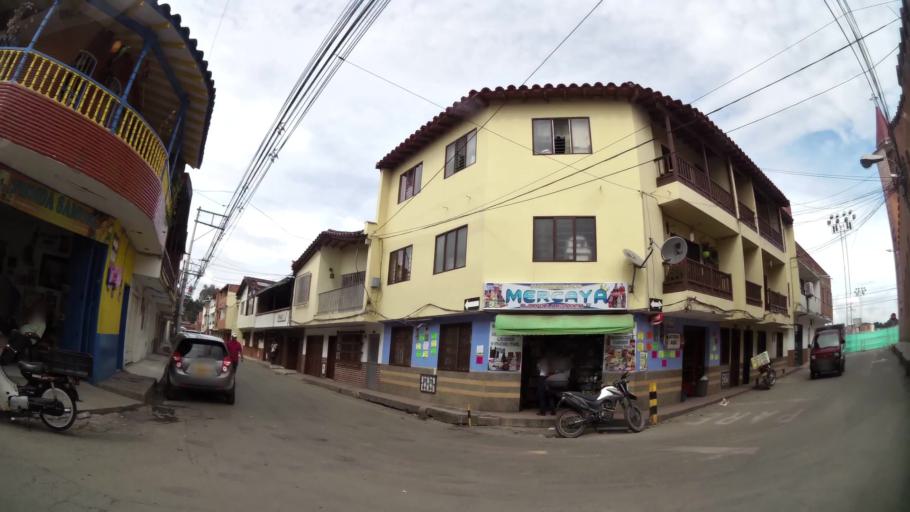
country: CO
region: Antioquia
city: Rionegro
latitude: 6.1587
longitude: -75.3728
